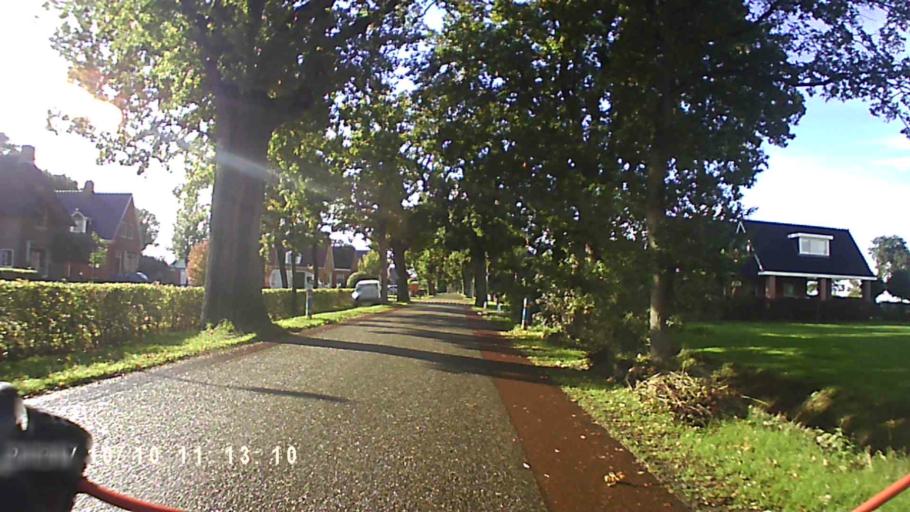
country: NL
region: Friesland
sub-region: Gemeente Smallingerland
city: Drachtstercompagnie
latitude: 53.1096
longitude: 6.2054
